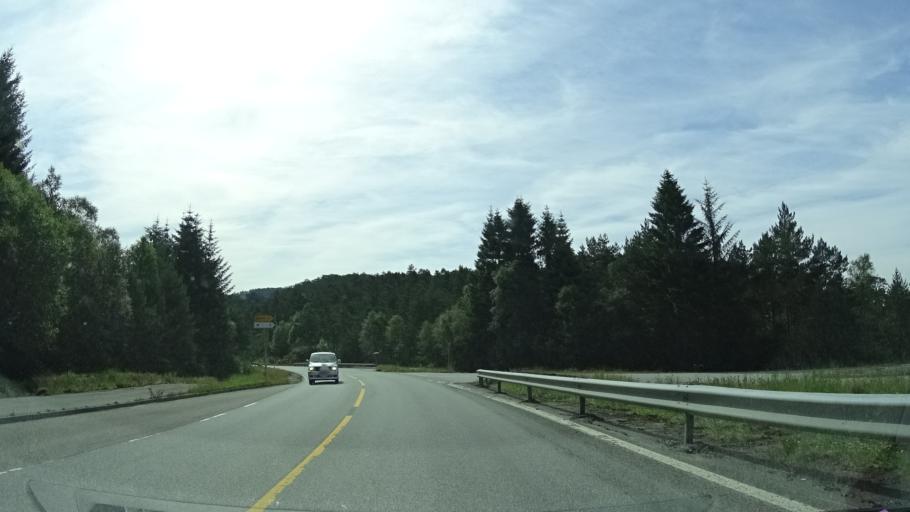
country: NO
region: Hordaland
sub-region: Bomlo
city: Mosterhamn
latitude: 59.6369
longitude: 5.4769
